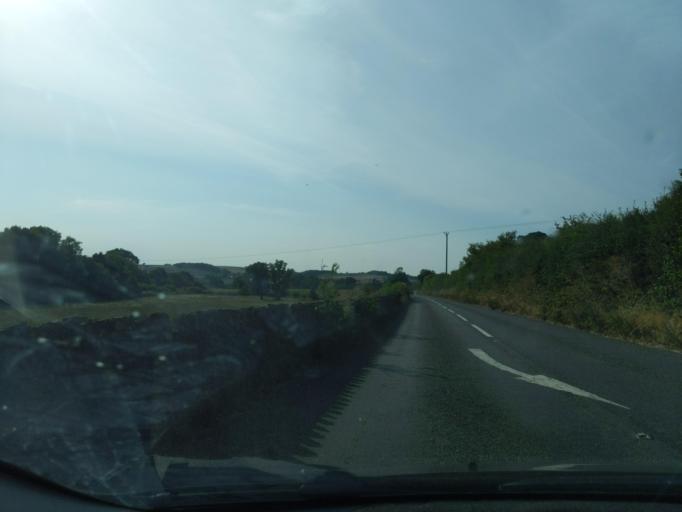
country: GB
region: England
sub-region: Devon
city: Winkleigh
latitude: 50.9048
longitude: -3.8856
